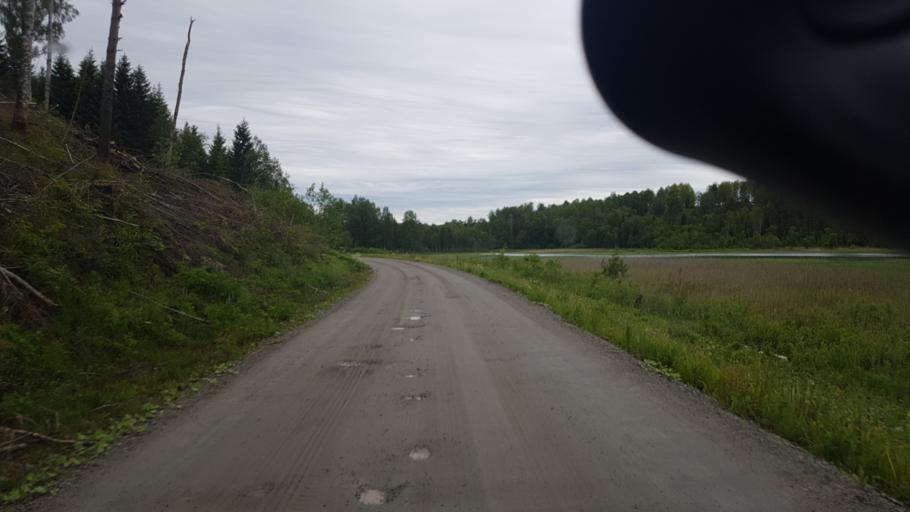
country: NO
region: Ostfold
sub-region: Romskog
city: Romskog
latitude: 59.6756
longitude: 11.9329
